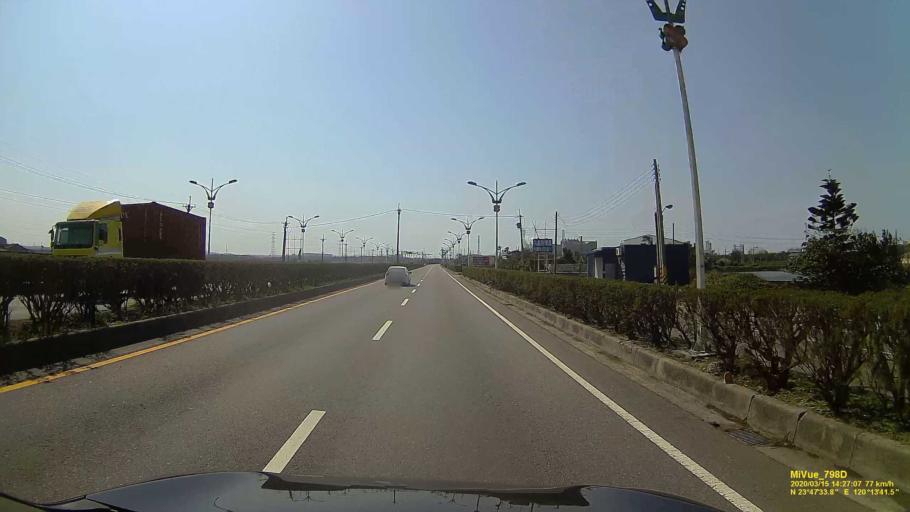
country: TW
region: Taiwan
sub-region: Yunlin
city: Douliu
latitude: 23.7927
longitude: 120.2286
